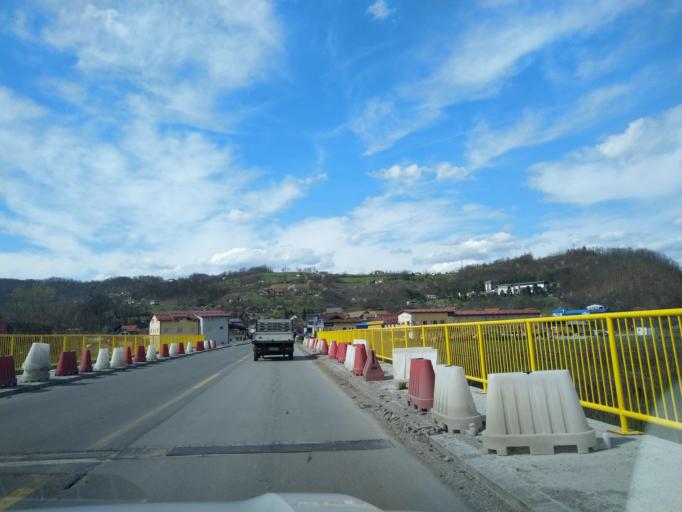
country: RS
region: Central Serbia
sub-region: Zlatiborski Okrug
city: Arilje
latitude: 43.7611
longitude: 20.0964
